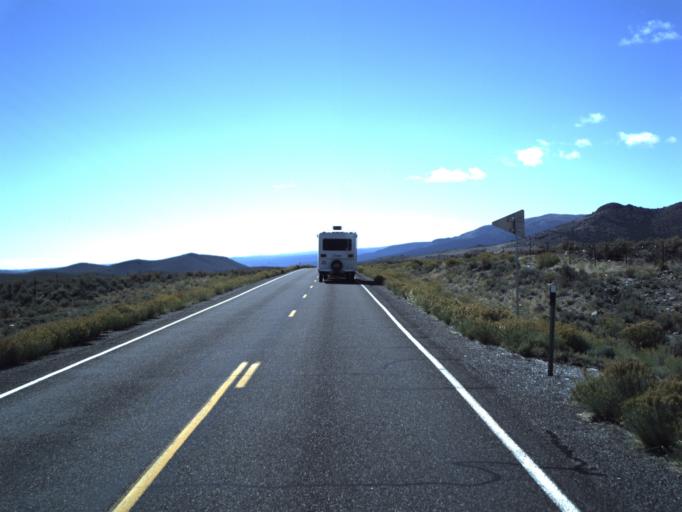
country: US
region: Utah
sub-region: Piute County
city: Junction
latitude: 38.3340
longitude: -111.9563
